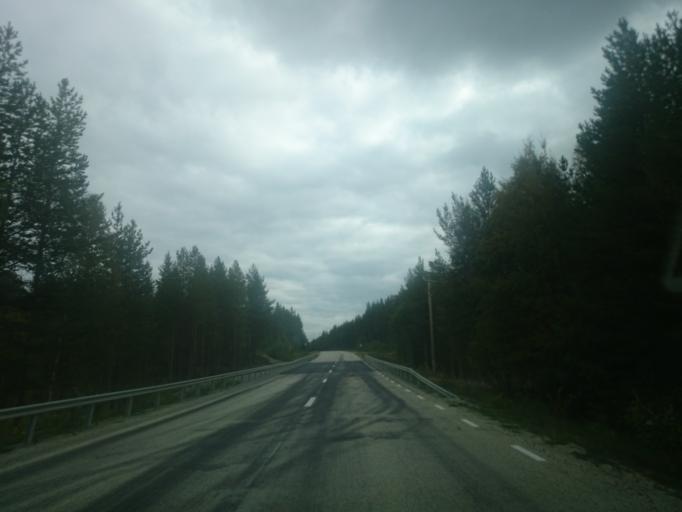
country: SE
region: Jaemtland
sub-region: Harjedalens Kommun
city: Sveg
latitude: 62.4078
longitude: 13.6944
